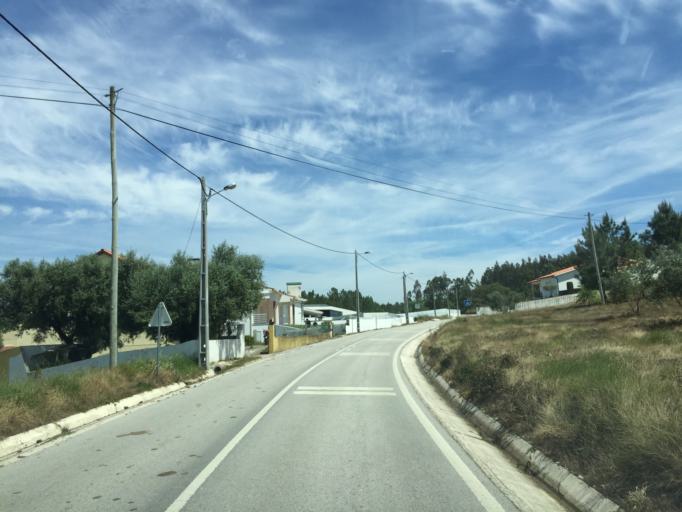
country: PT
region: Coimbra
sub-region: Soure
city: Soure
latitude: 40.0534
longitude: -8.6676
